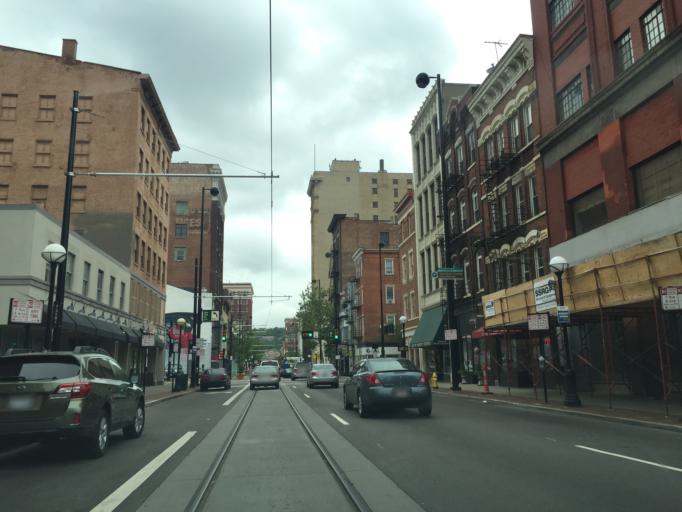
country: US
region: Kentucky
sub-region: Campbell County
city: Newport
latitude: 39.1044
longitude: -84.5104
